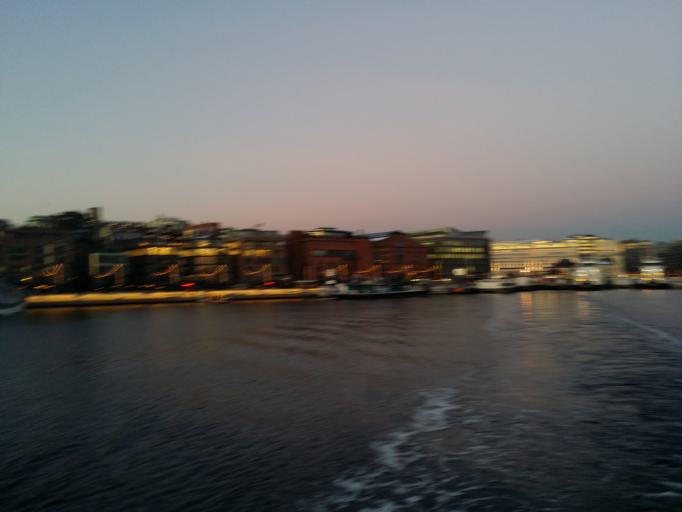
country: NO
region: Oslo
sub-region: Oslo
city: Oslo
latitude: 59.9075
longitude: 10.7278
